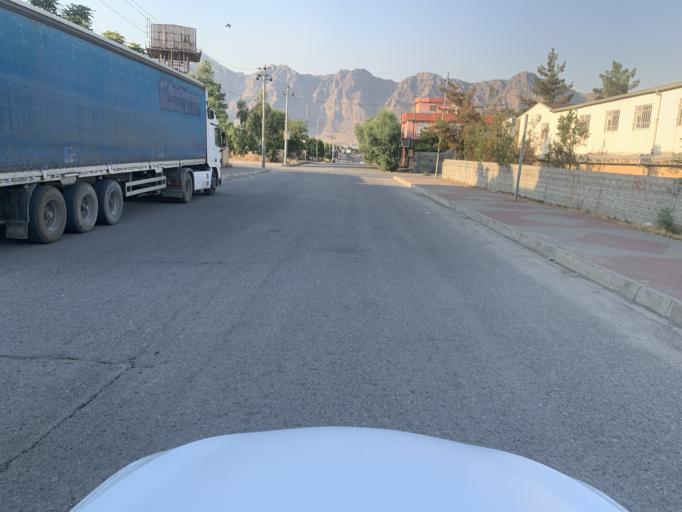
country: IQ
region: As Sulaymaniyah
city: Raniye
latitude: 36.2423
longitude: 44.8791
